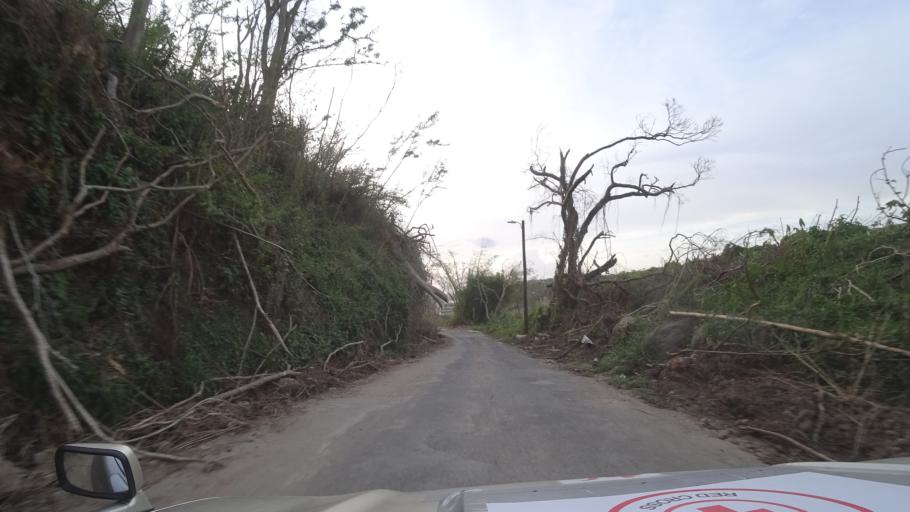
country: DM
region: Saint George
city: Roseau
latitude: 15.3007
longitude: -61.3795
